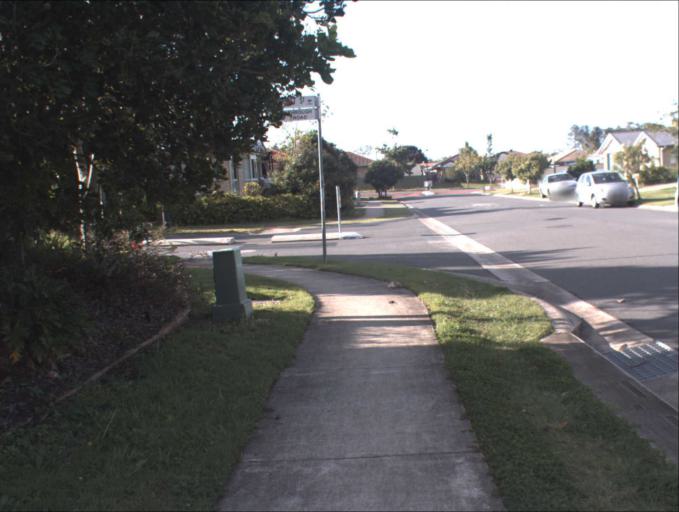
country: AU
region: Queensland
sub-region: Logan
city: Logan Reserve
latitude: -27.6977
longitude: 153.0946
